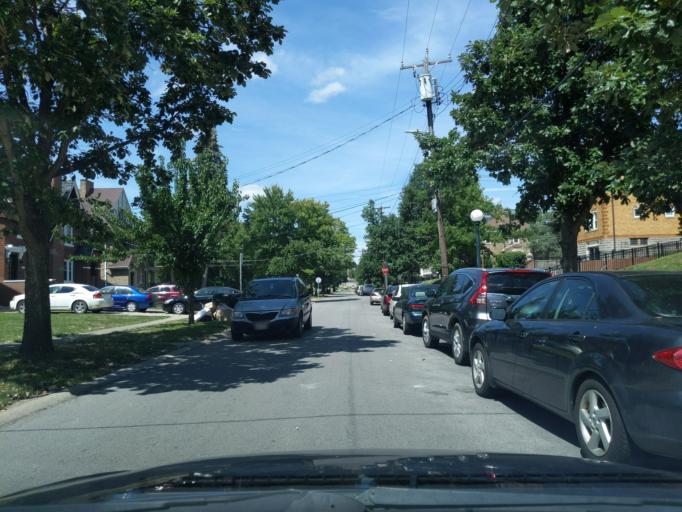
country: US
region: Ohio
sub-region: Hamilton County
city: Saint Bernard
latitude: 39.1324
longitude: -84.5219
